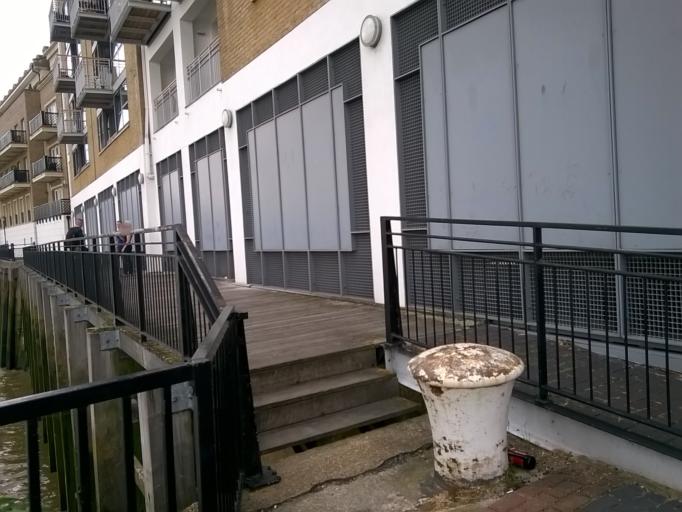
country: GB
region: England
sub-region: Greater London
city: Poplar
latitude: 51.5096
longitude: -0.0381
